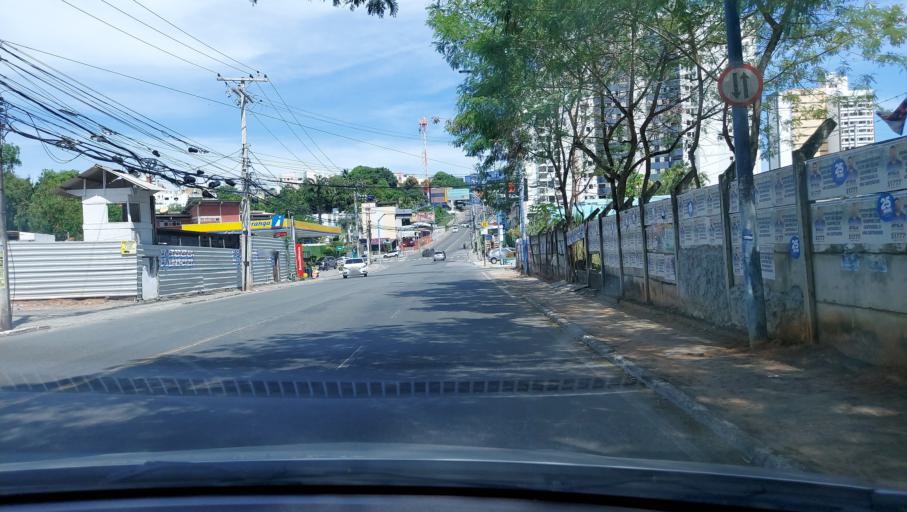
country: BR
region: Bahia
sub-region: Salvador
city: Salvador
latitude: -12.9802
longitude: -38.4497
